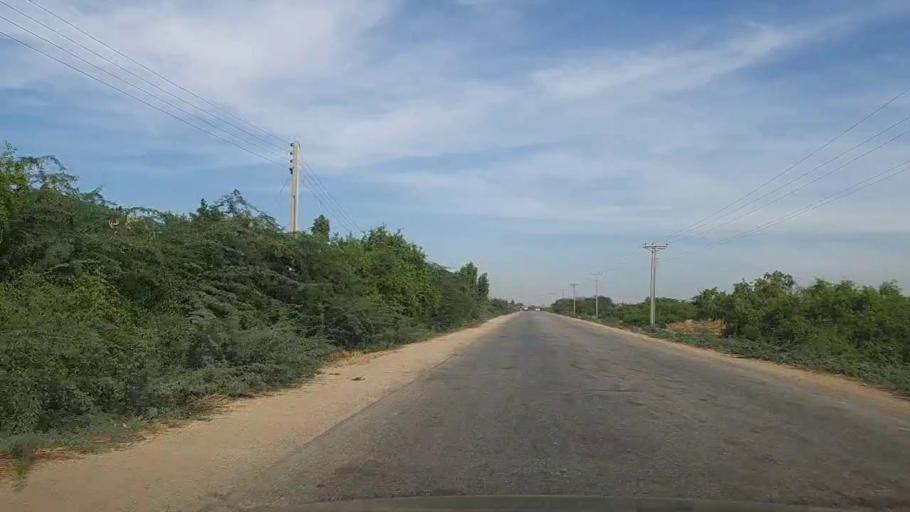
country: PK
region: Sindh
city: Daro Mehar
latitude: 24.9306
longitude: 68.1043
